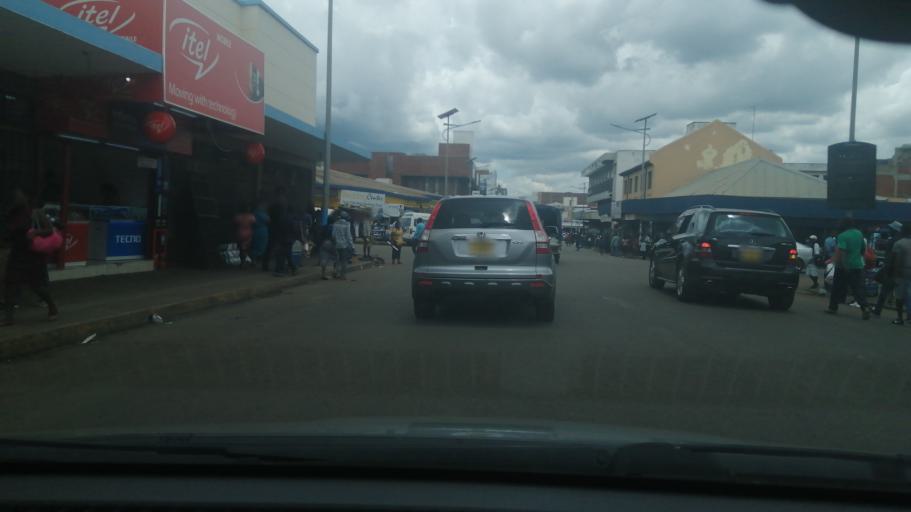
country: ZW
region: Harare
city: Harare
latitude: -17.8339
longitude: 31.0438
